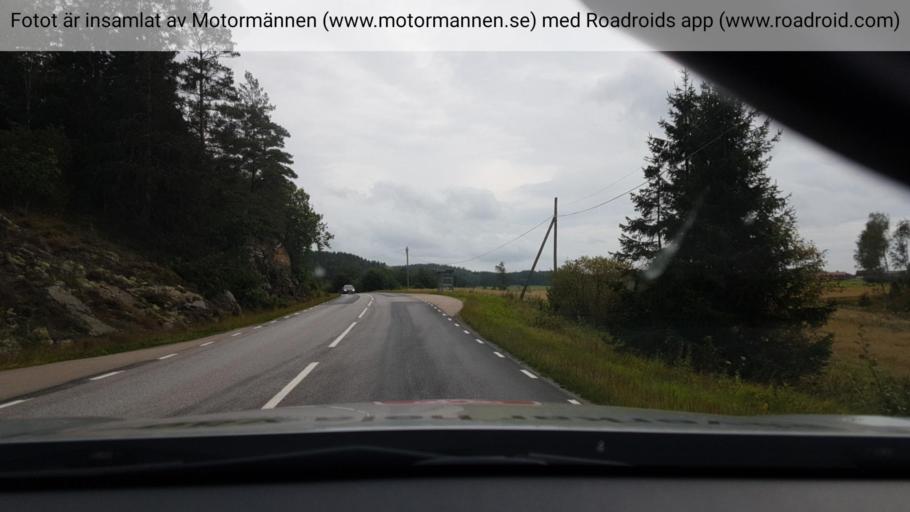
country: SE
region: Vaestra Goetaland
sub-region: Sotenas Kommun
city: Hunnebostrand
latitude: 58.5579
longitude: 11.4020
